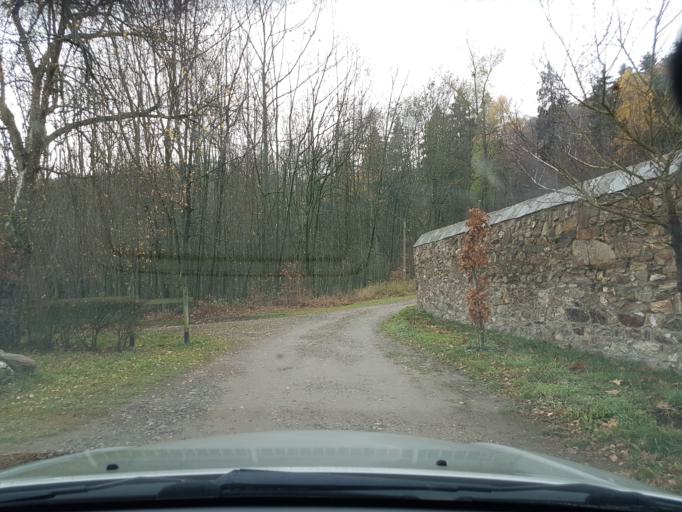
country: DE
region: Hesse
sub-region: Regierungsbezirk Darmstadt
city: Kiedrich
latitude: 50.0478
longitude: 8.0431
